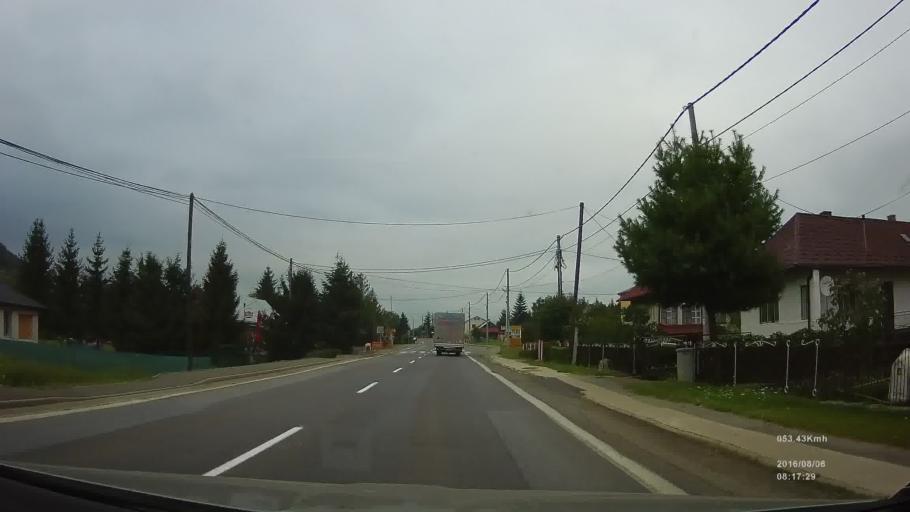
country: SK
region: Presovsky
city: Stropkov
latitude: 49.2200
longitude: 21.6386
